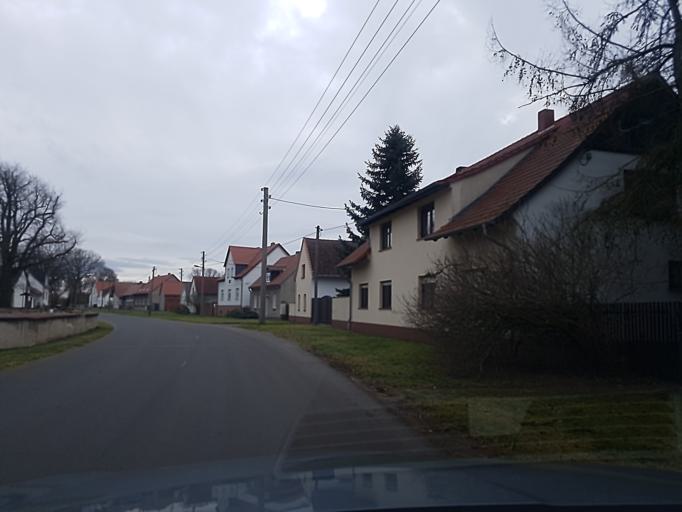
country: DE
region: Brandenburg
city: Schilda
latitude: 51.6204
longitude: 13.3551
